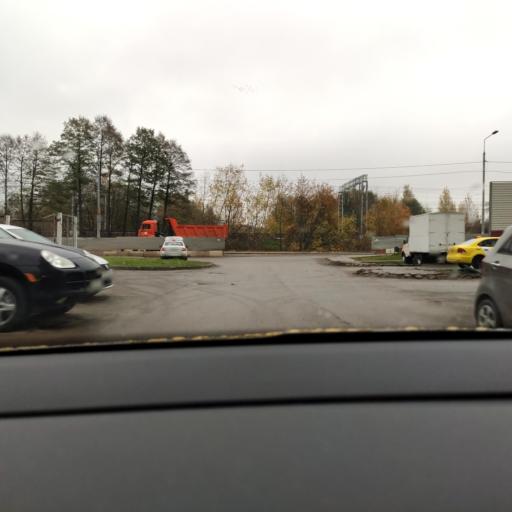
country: RU
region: Moskovskaya
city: Shcherbinka
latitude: 55.4955
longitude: 37.5563
